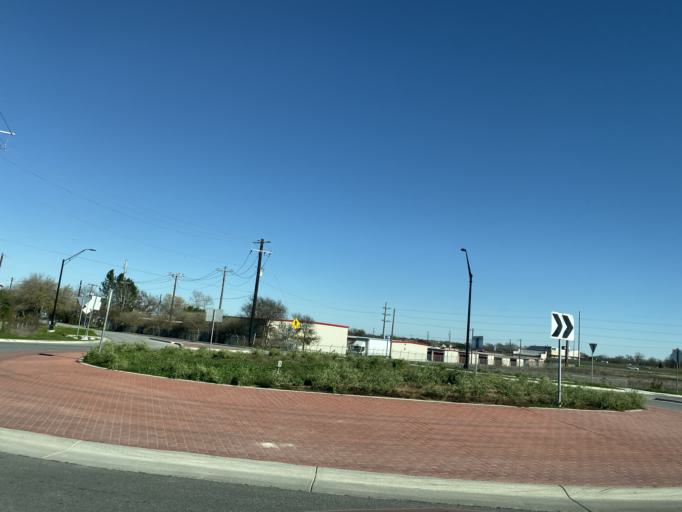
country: US
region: Texas
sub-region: Hays County
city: Kyle
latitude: 30.0008
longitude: -97.8716
